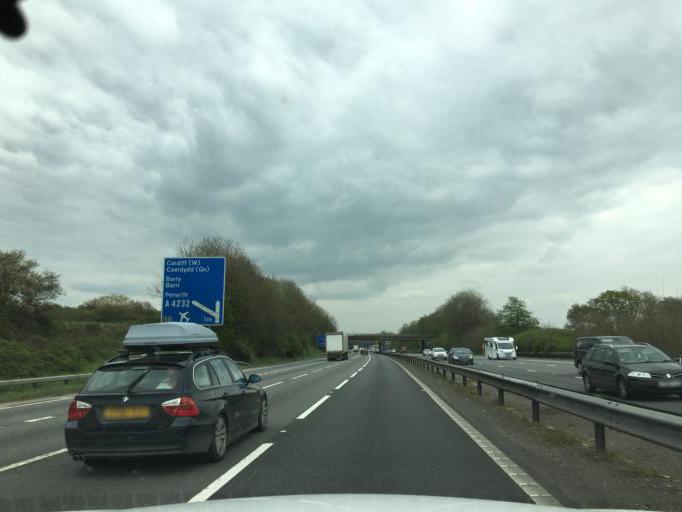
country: GB
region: Wales
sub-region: Rhondda Cynon Taf
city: Llantrisant
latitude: 51.5084
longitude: -3.3420
